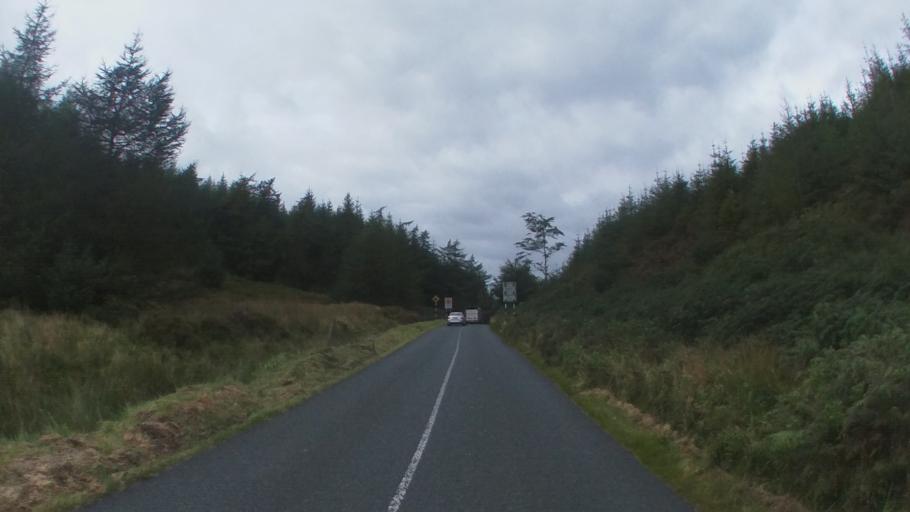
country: IE
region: Leinster
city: Ballinteer
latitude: 53.2386
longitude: -6.2862
